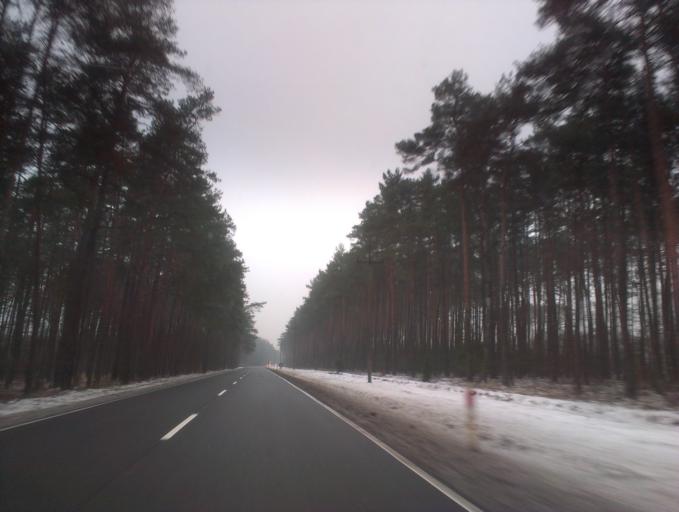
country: PL
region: Greater Poland Voivodeship
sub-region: Powiat zlotowski
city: Tarnowka
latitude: 53.3422
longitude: 16.7911
